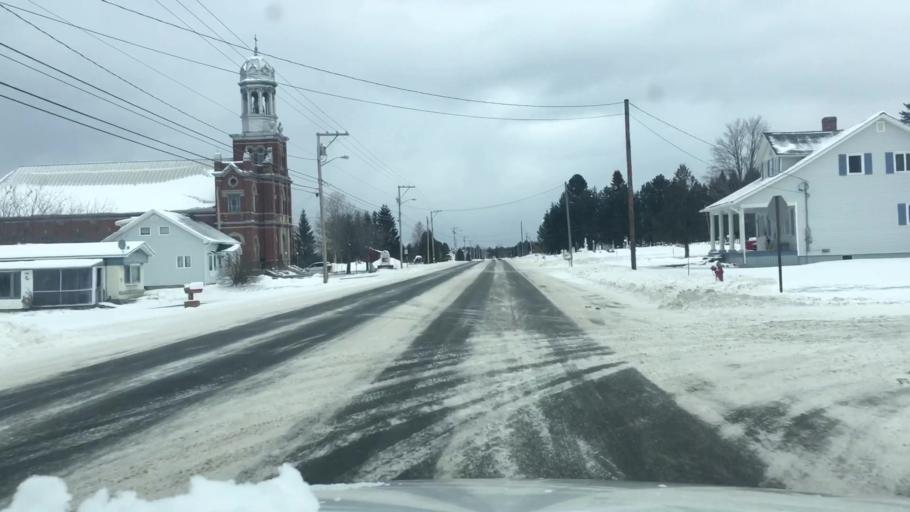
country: US
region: Maine
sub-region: Aroostook County
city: Madawaska
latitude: 47.3492
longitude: -68.2790
